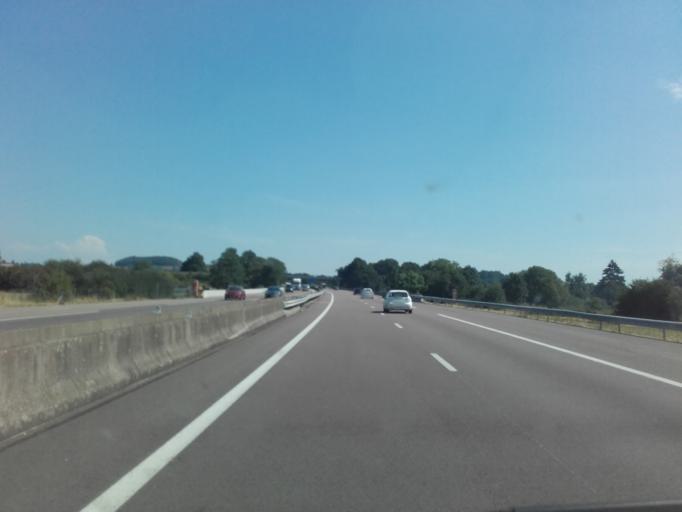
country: FR
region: Bourgogne
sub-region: Departement de la Cote-d'Or
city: Pouilly-en-Auxois
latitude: 47.2645
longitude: 4.5182
